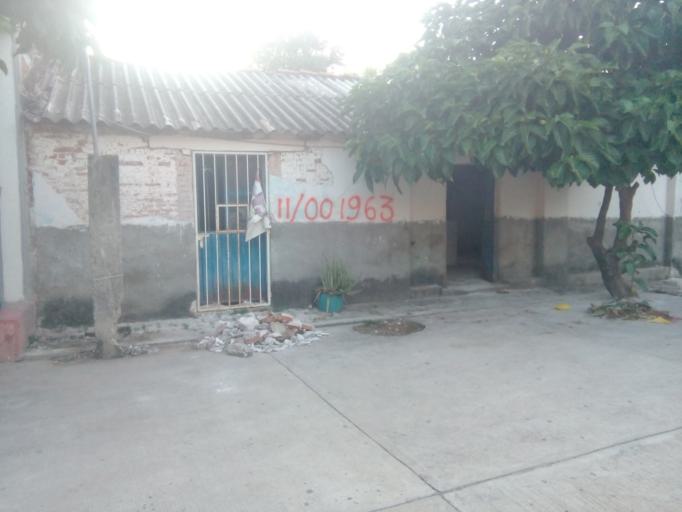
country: MX
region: Oaxaca
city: San Jeronimo Ixtepec
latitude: 16.5684
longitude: -95.1024
